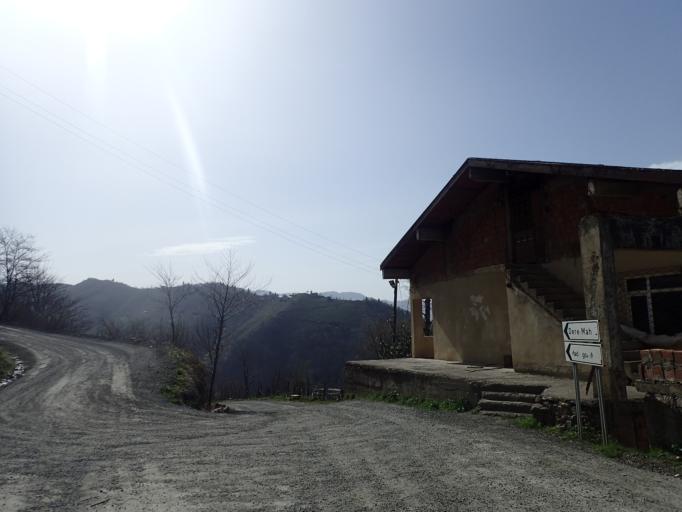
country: TR
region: Ordu
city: Kabaduz
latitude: 40.8196
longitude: 37.8760
